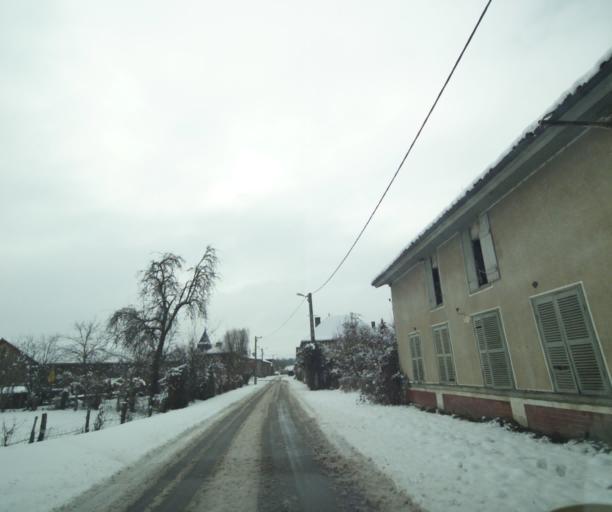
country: FR
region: Champagne-Ardenne
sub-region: Departement de la Haute-Marne
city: Montier-en-Der
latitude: 48.5134
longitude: 4.6991
